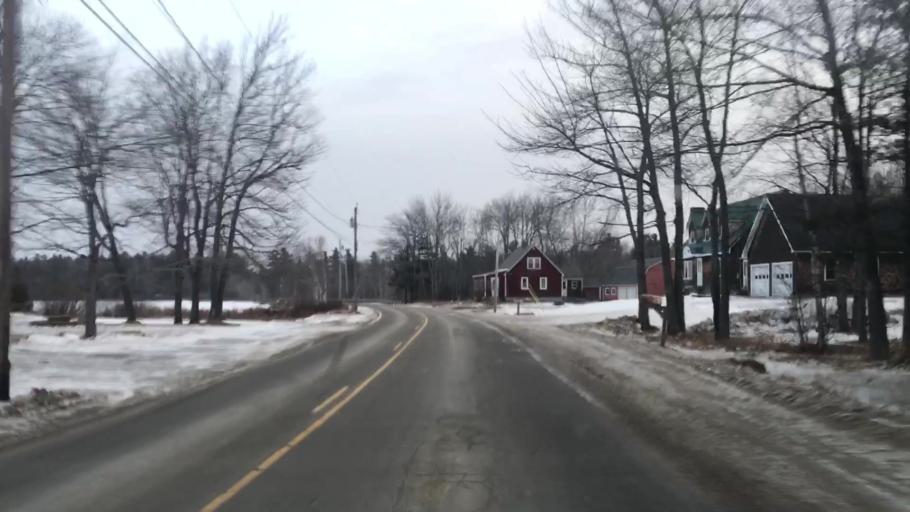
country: US
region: Maine
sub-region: Hancock County
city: Ellsworth
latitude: 44.6121
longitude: -68.3881
